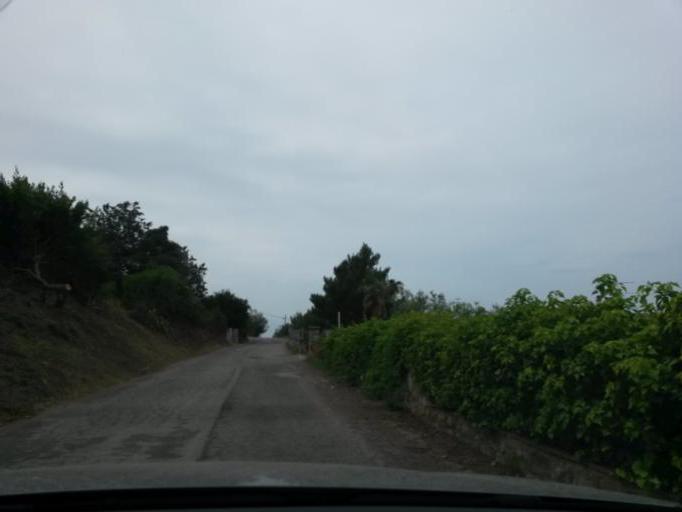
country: IT
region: Tuscany
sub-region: Provincia di Livorno
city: Capoliveri
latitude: 42.7355
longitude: 10.3719
